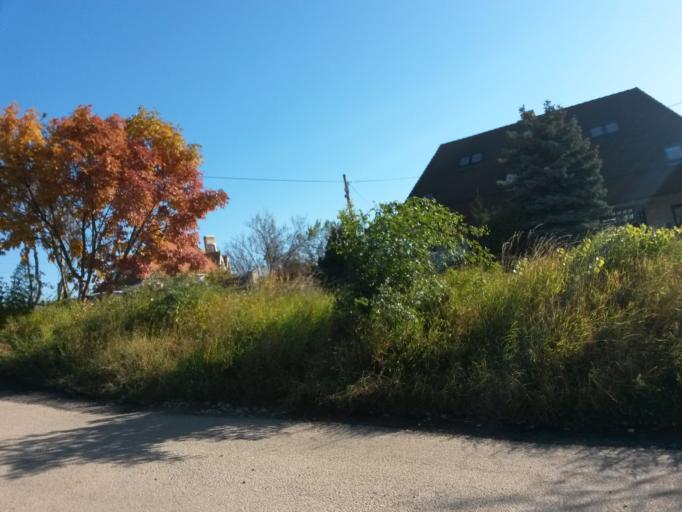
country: HU
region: Pest
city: Budaors
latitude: 47.4758
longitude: 18.9859
